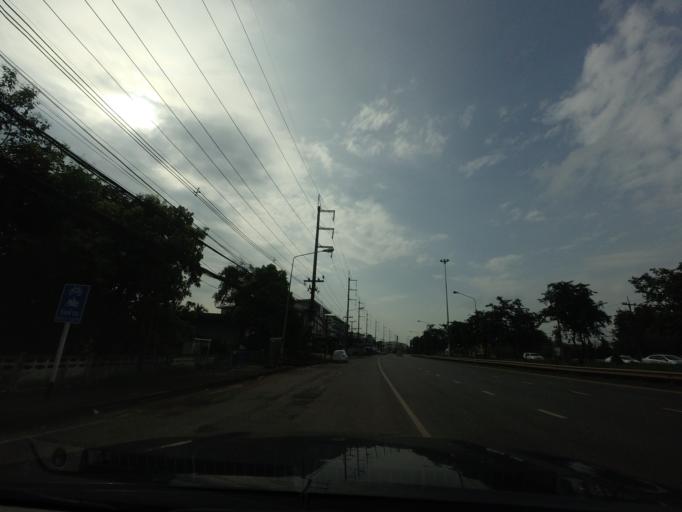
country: TH
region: Nong Khai
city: Nong Khai
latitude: 17.8641
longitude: 102.7485
